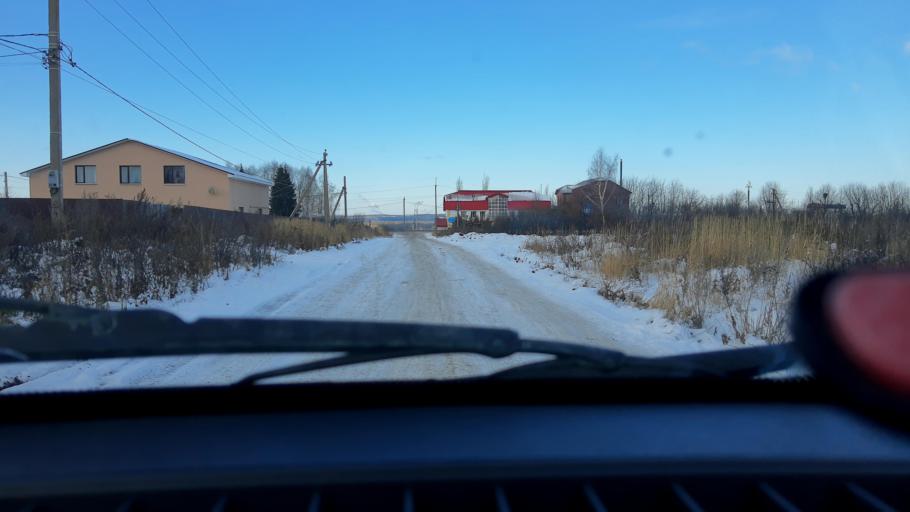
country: RU
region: Bashkortostan
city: Iglino
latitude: 54.7927
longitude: 56.2447
